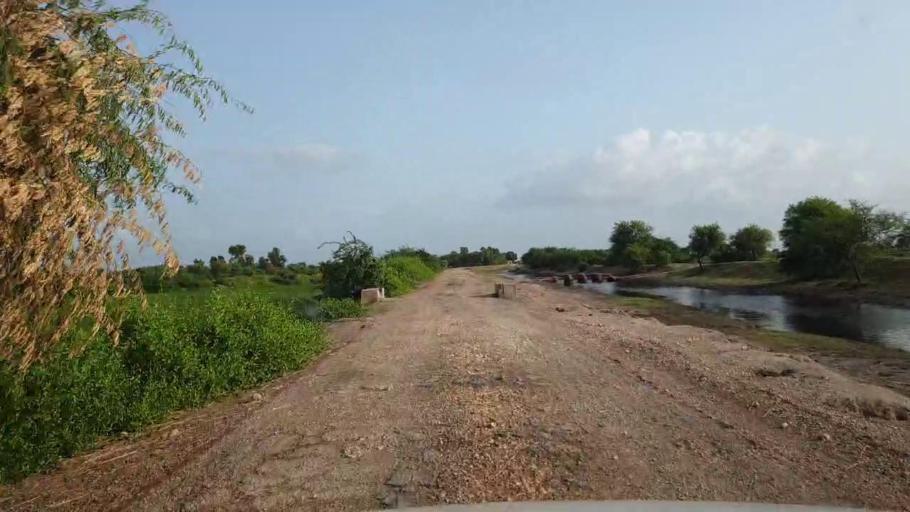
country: PK
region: Sindh
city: Kario
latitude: 24.8399
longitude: 68.6523
